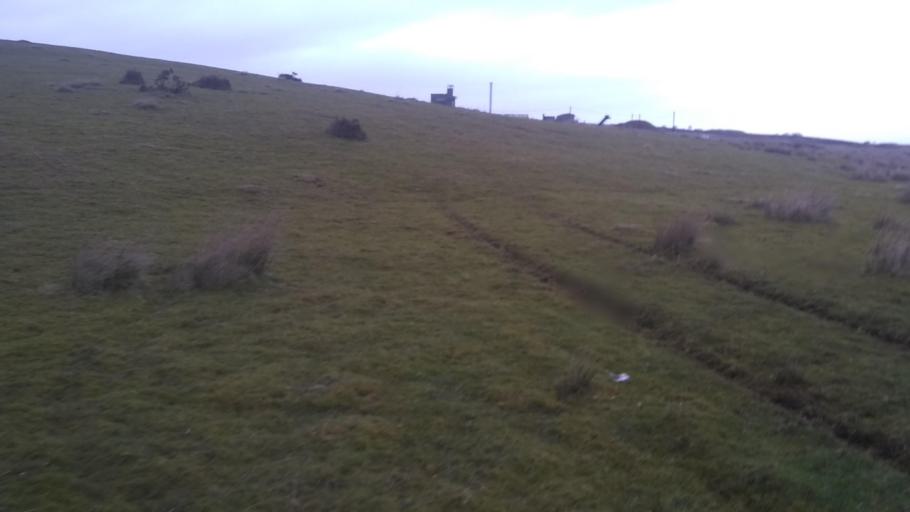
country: GB
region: England
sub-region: Worcestershire
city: Tenbury Wells
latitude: 52.3773
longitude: -2.5912
